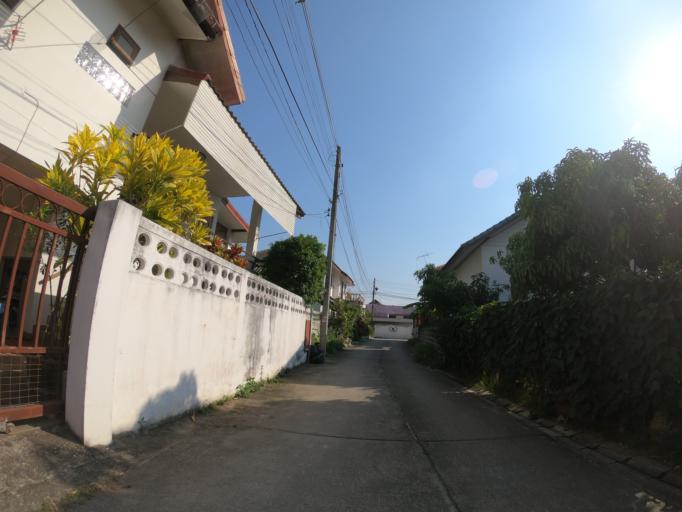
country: TH
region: Chiang Mai
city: Chiang Mai
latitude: 18.8209
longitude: 99.0024
